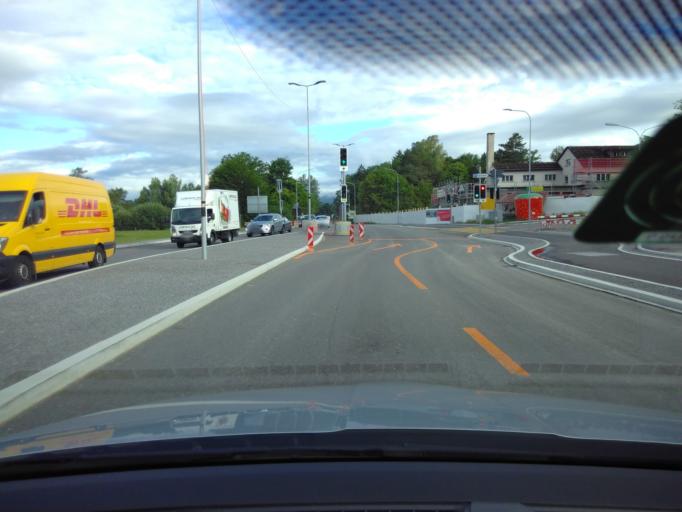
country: CH
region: Zurich
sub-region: Bezirk Zuerich
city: Zuerich (Kreis 10) / Ruetihof
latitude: 47.4276
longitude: 8.4907
